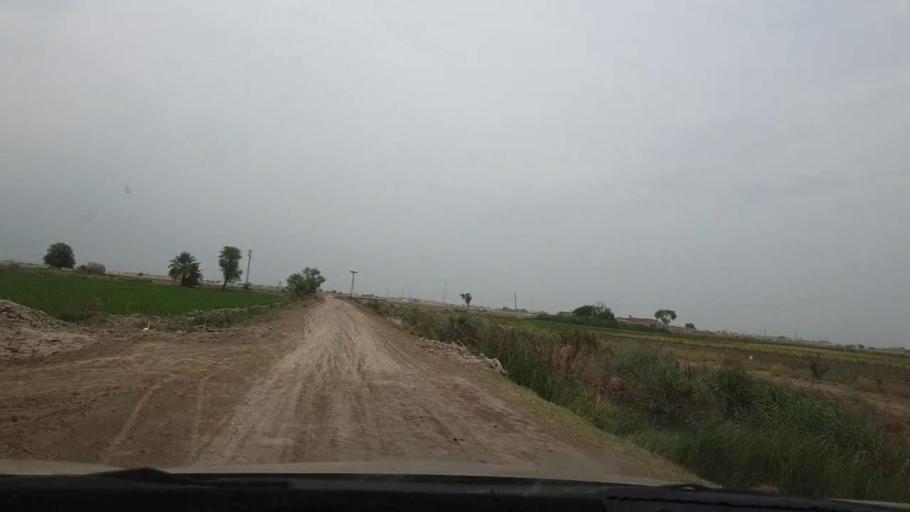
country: PK
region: Sindh
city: Ratodero
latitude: 27.7734
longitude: 68.2771
